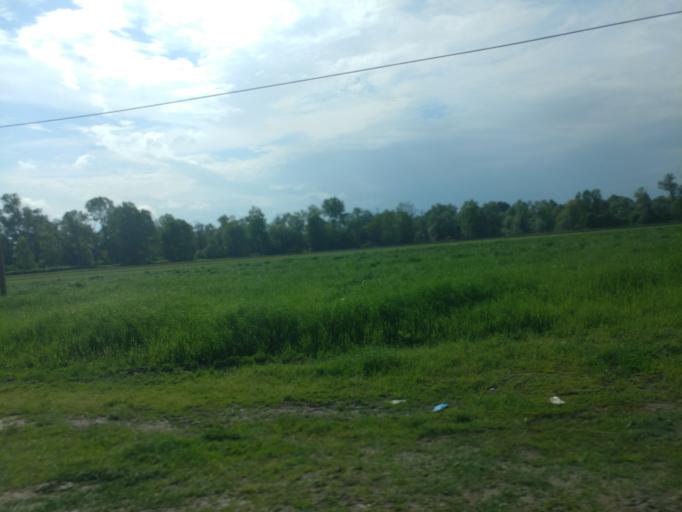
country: IT
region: Piedmont
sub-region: Provincia di Cuneo
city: Faule
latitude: 44.8126
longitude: 7.5857
